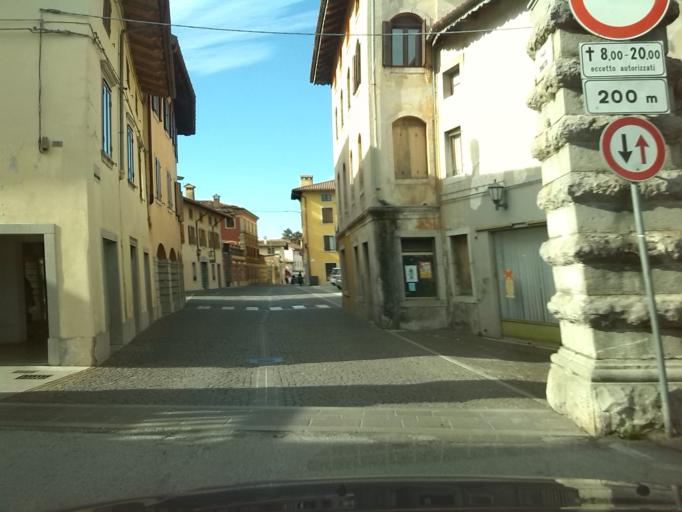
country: IT
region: Friuli Venezia Giulia
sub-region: Provincia di Udine
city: Cividale del Friuli
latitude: 46.0899
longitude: 13.4331
